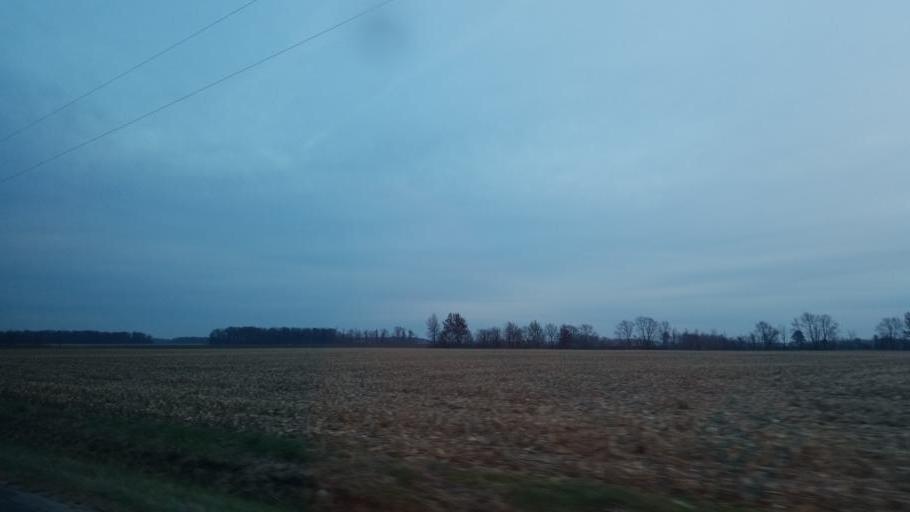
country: US
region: Indiana
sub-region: Adams County
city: Decatur
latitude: 40.7882
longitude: -84.9741
